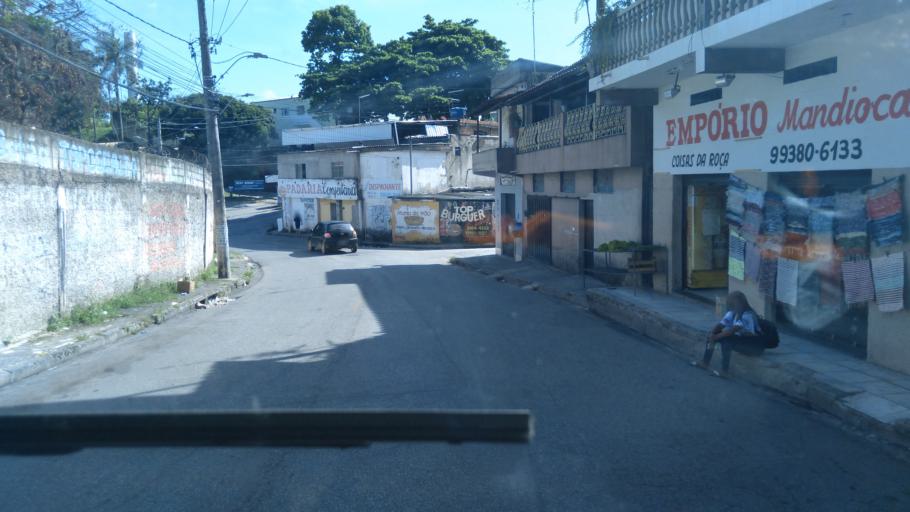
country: BR
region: Minas Gerais
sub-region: Santa Luzia
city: Santa Luzia
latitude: -19.8497
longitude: -43.8858
